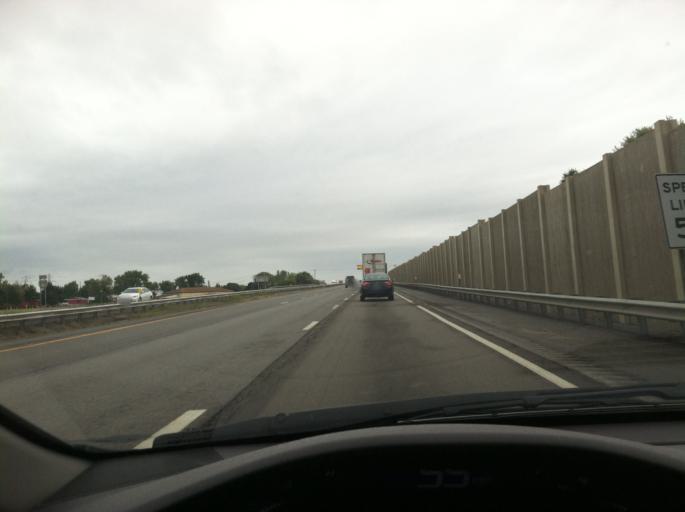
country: US
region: New York
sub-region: Erie County
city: Blasdell
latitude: 42.7970
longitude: -78.8163
